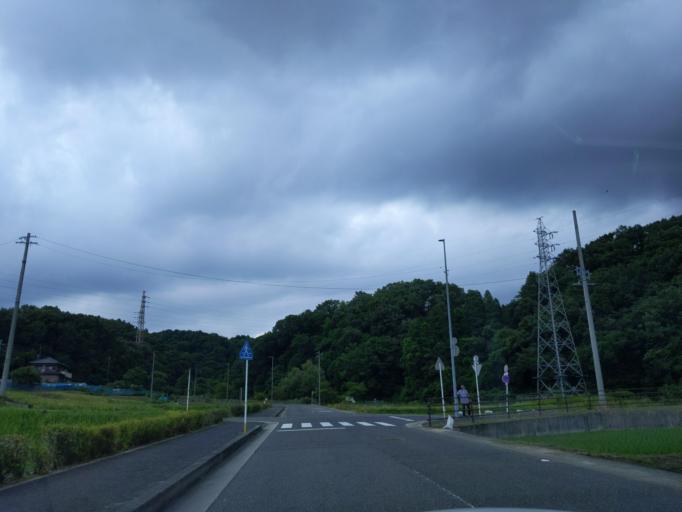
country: JP
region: Aichi
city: Seto
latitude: 35.1901
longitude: 137.1099
